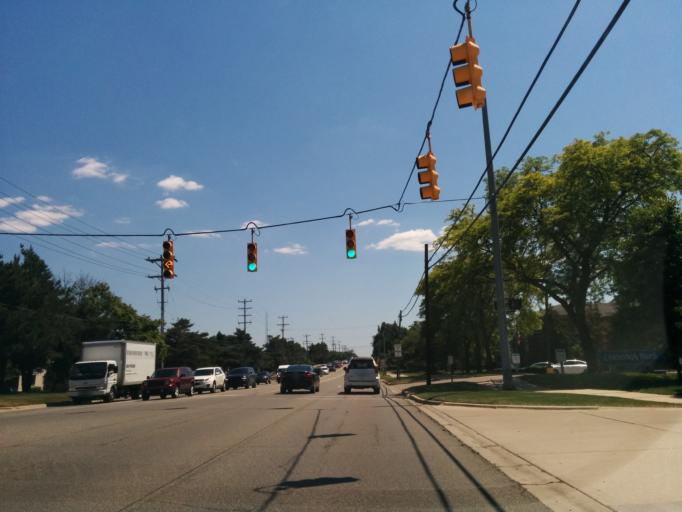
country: US
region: Michigan
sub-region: Oakland County
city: Orchard Lake
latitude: 42.5735
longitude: -83.3622
